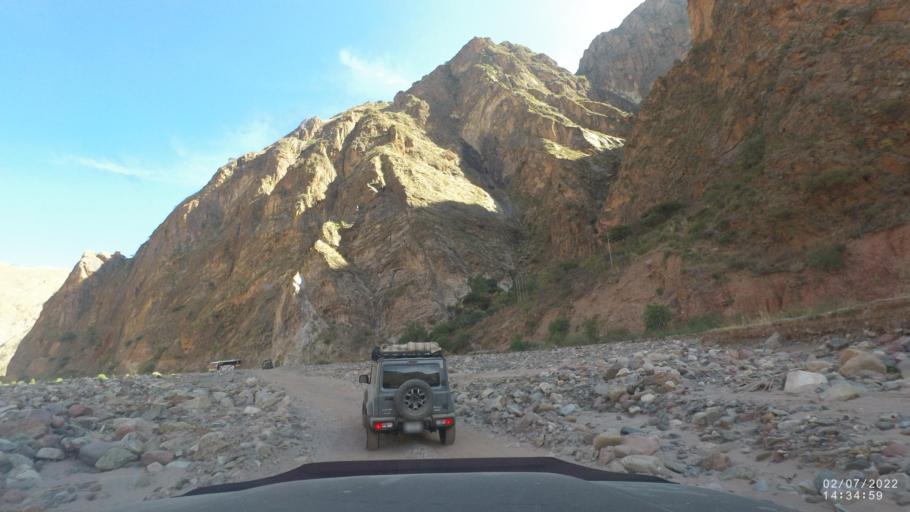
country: BO
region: Cochabamba
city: Irpa Irpa
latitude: -17.8397
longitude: -66.4175
